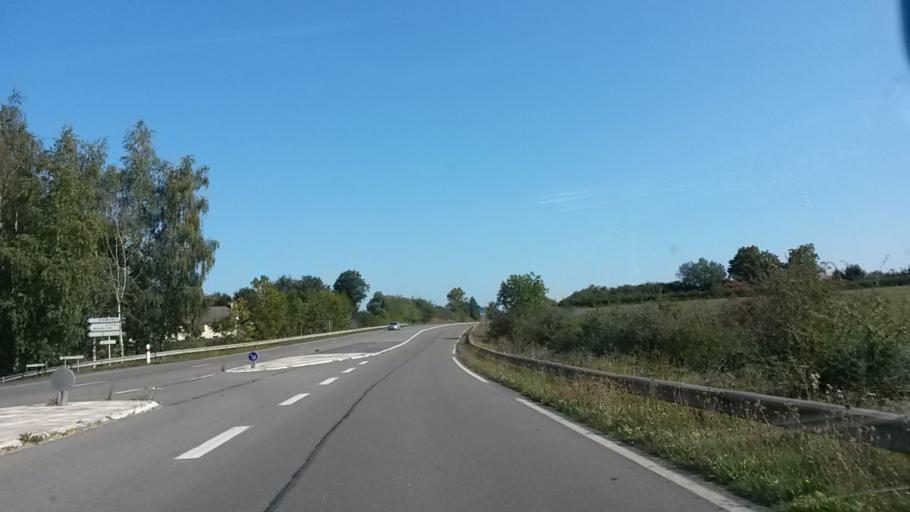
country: FR
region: Picardie
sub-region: Departement de l'Aisne
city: La Flamengrie
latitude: 50.0503
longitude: 3.9277
